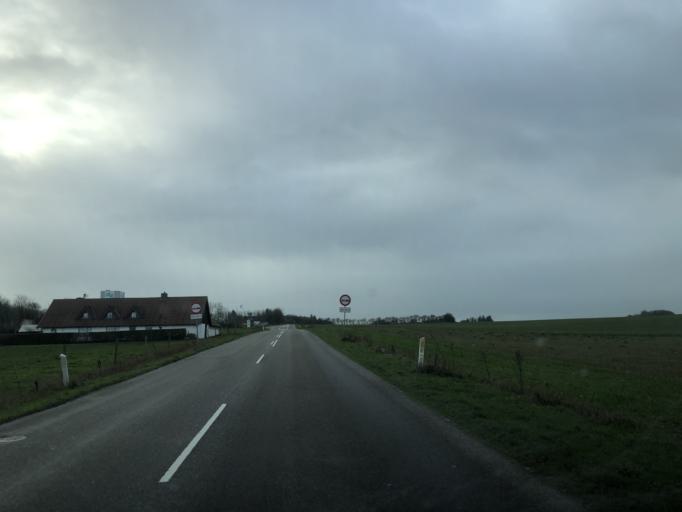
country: DK
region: North Denmark
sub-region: Rebild Kommune
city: Stovring
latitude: 56.8858
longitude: 9.7839
